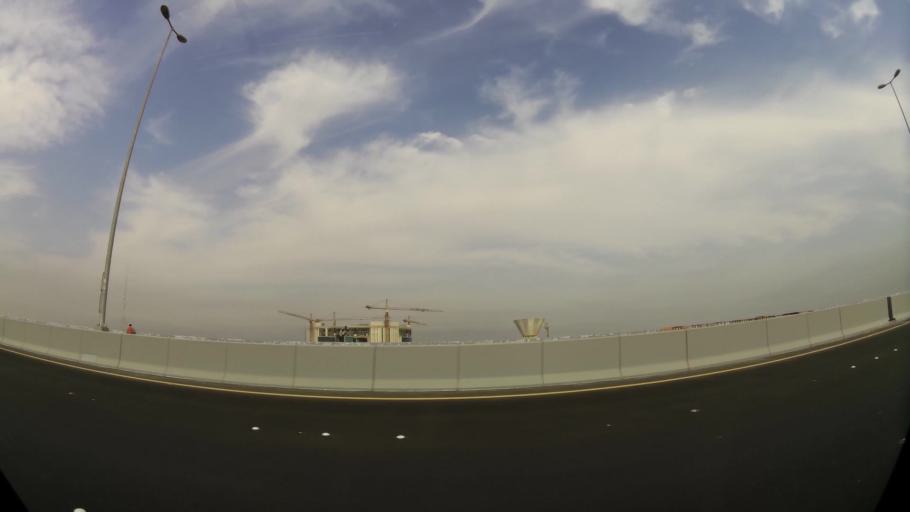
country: KW
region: Al Asimah
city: Ar Rabiyah
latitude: 29.3219
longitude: 47.8876
